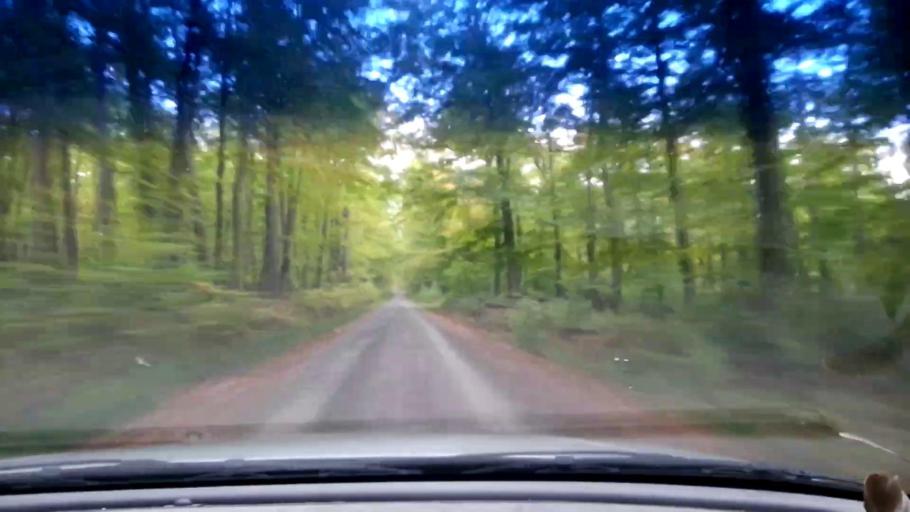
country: DE
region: Bavaria
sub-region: Upper Franconia
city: Burgwindheim
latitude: 49.8516
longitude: 10.6407
